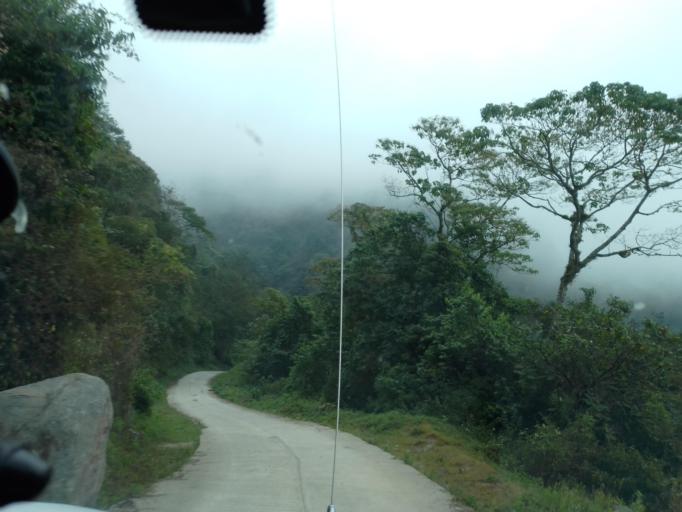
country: MX
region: Chiapas
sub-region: Union Juarez
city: Santo Domingo
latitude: 15.0935
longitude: -92.0961
